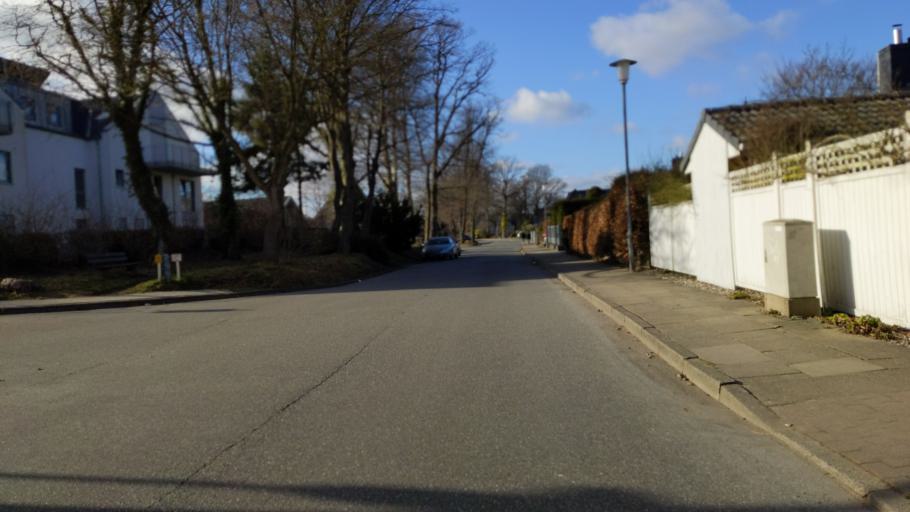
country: DE
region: Schleswig-Holstein
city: Scharbeutz
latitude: 54.0185
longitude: 10.7602
